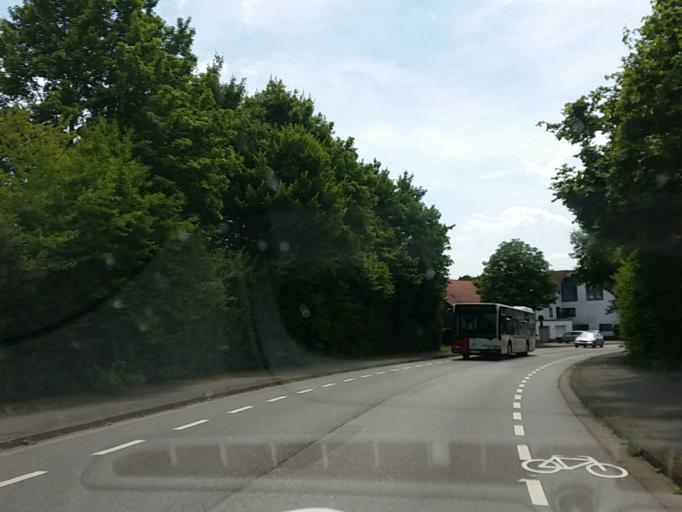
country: DE
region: Saarland
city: Schmelz
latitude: 49.4287
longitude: 6.8471
